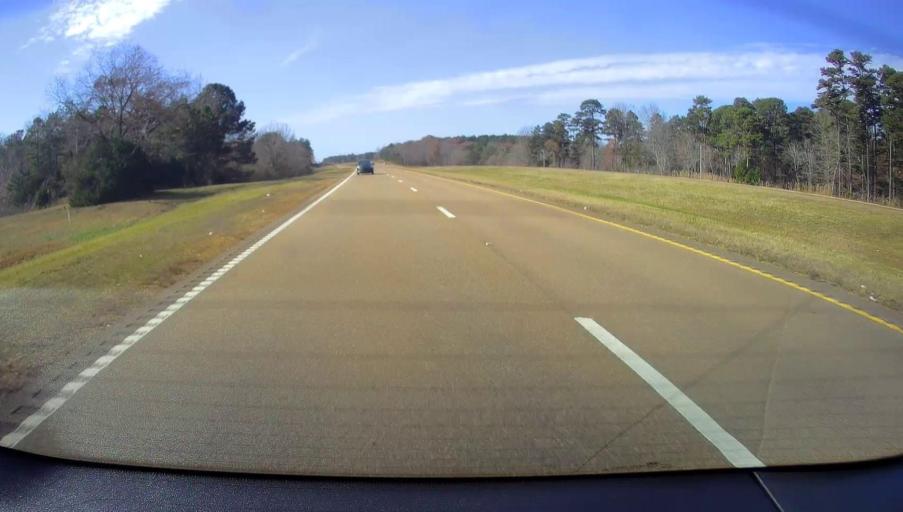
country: US
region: Mississippi
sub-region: Benton County
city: Ashland
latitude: 34.9542
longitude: -89.0231
